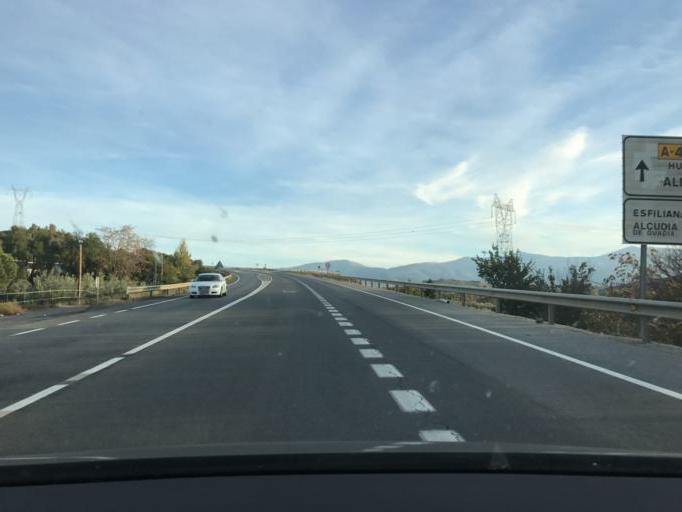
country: ES
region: Andalusia
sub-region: Provincia de Granada
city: Guadix
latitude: 37.2758
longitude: -3.1106
